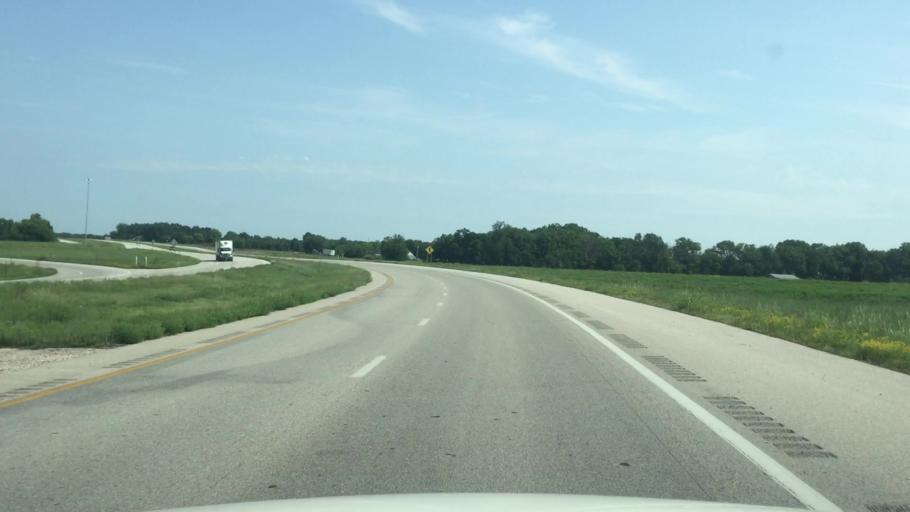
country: US
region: Kansas
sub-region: Montgomery County
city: Coffeyville
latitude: 37.0466
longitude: -95.5817
